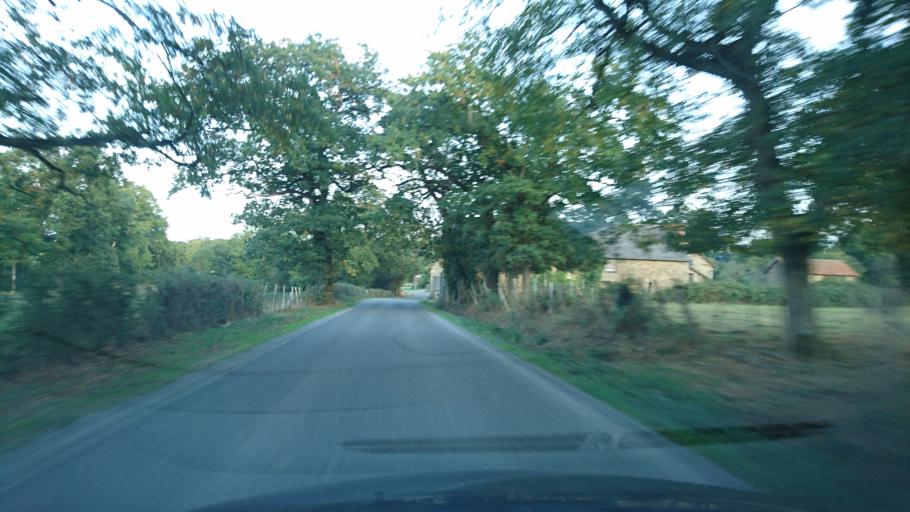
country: FR
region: Brittany
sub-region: Departement d'Ille-et-Vilaine
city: Bains-sur-Oust
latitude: 47.7064
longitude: -2.0593
